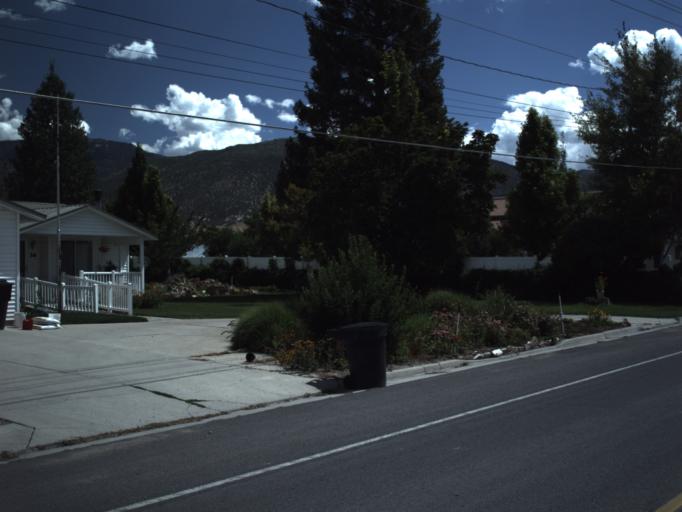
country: US
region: Utah
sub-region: Sanpete County
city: Ephraim
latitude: 39.3609
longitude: -111.5772
